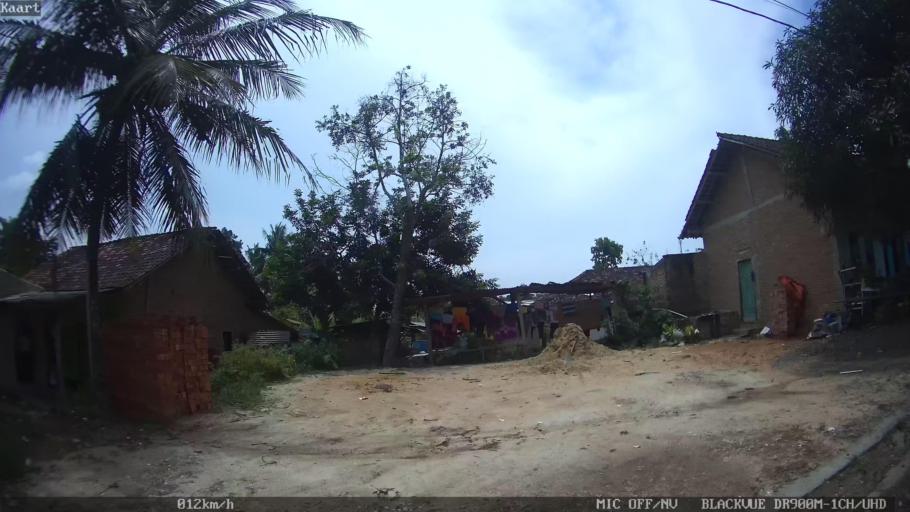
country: ID
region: Lampung
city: Bandarlampung
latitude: -5.4114
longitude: 105.2084
